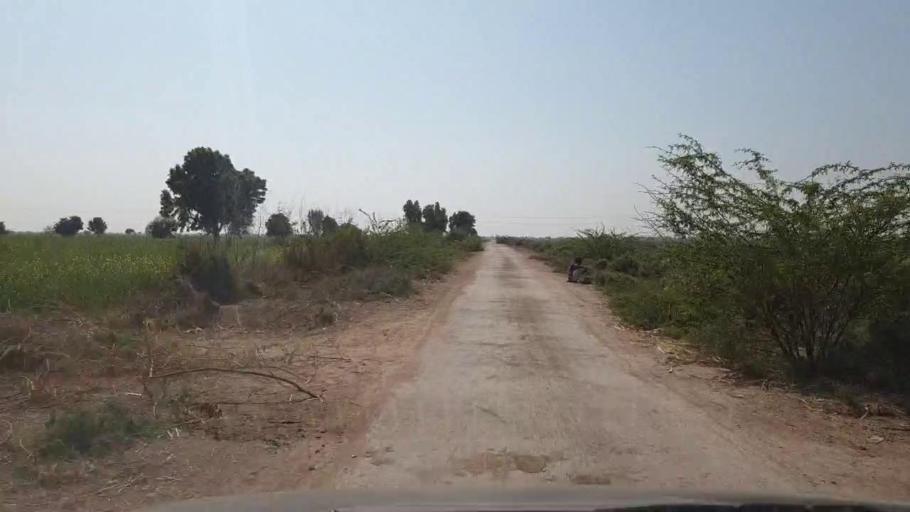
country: PK
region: Sindh
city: Digri
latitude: 25.1947
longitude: 69.2249
